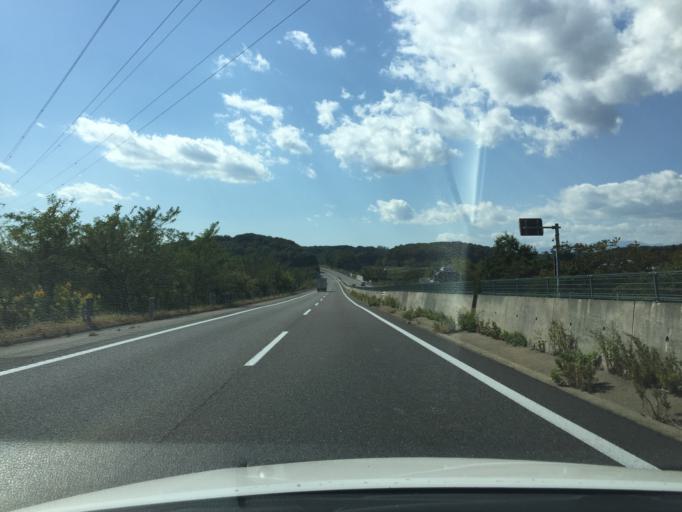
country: JP
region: Fukushima
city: Sukagawa
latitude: 37.2252
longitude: 140.3191
